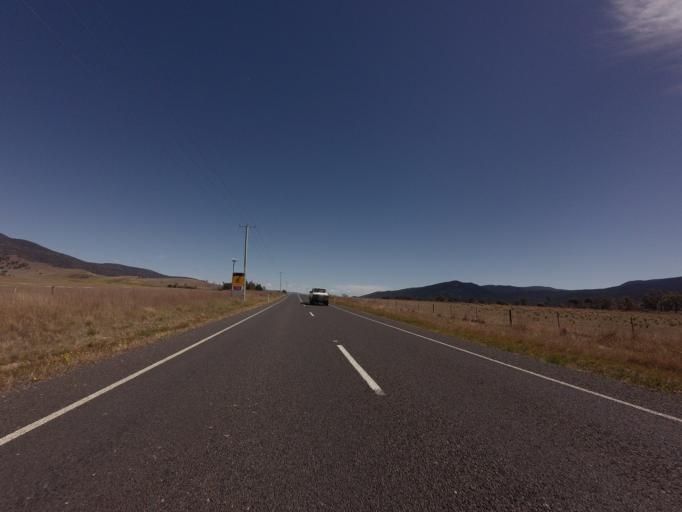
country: AU
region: Tasmania
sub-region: Break O'Day
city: St Helens
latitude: -41.7115
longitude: 147.8406
